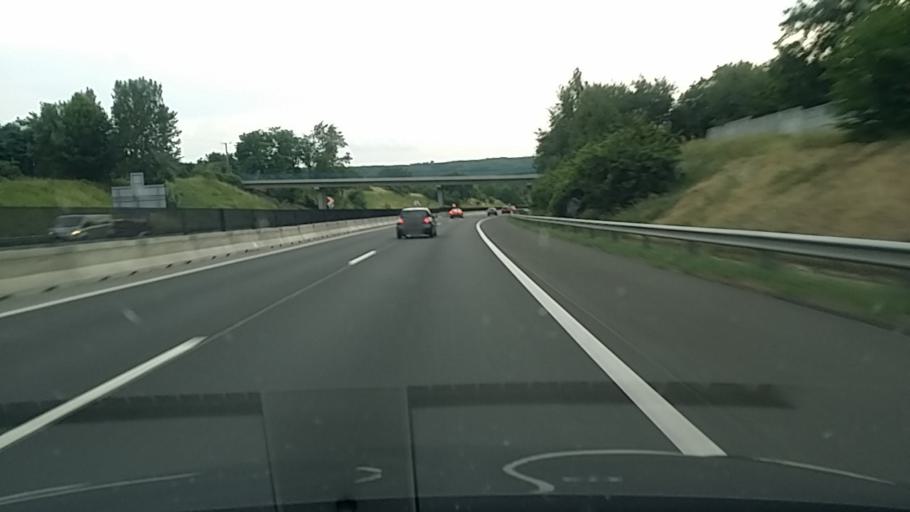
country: HU
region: Pest
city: Mogyorod
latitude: 47.5974
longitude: 19.2466
